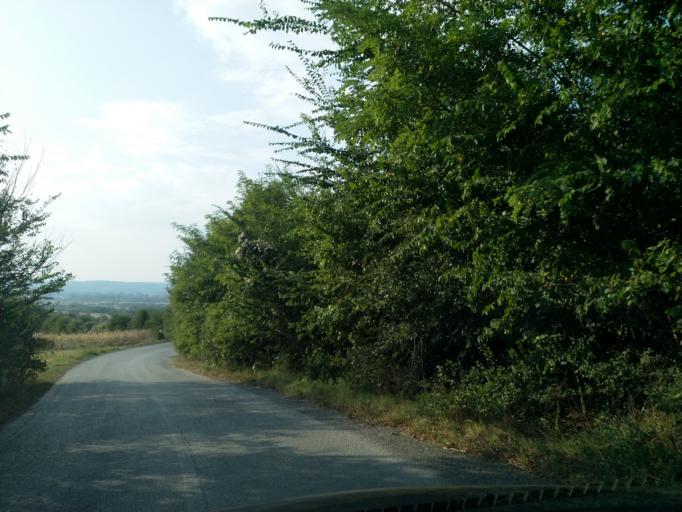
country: RS
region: Central Serbia
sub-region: Pomoravski Okrug
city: Paracin
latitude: 43.8443
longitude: 21.5283
